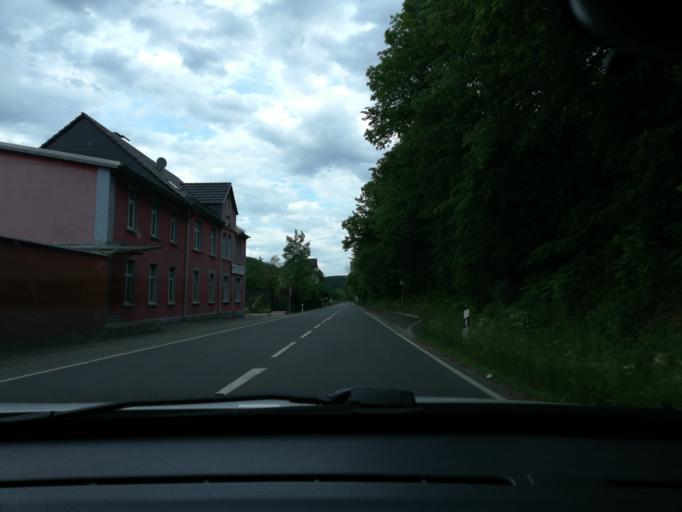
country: DE
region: North Rhine-Westphalia
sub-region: Regierungsbezirk Arnsberg
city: Schalksmuhle
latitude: 51.2688
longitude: 7.5210
